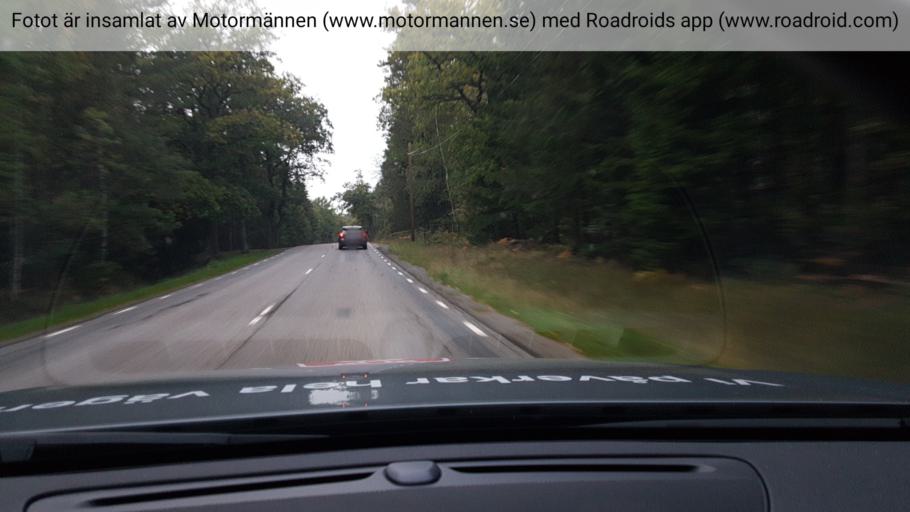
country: SE
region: Stockholm
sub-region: Haninge Kommun
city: Haninge
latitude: 59.1191
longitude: 18.1874
